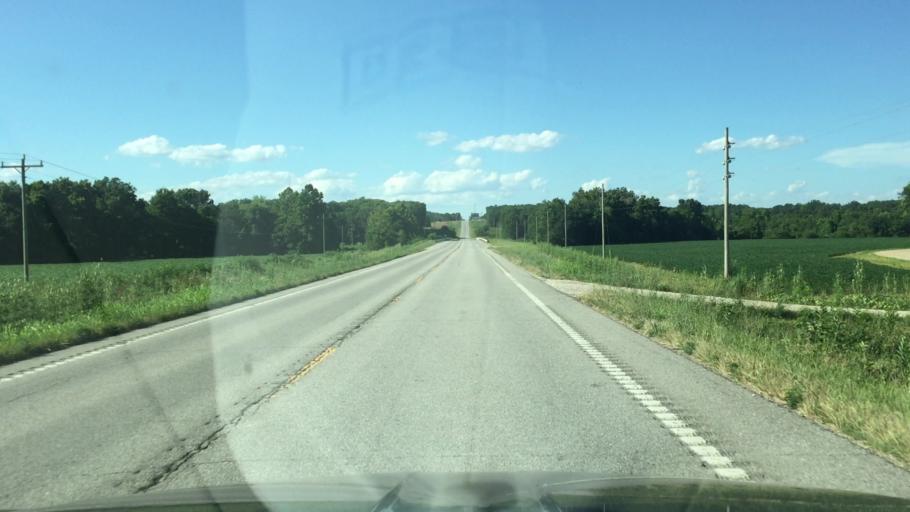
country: US
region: Missouri
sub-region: Moniteau County
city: Tipton
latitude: 38.5489
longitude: -92.7976
